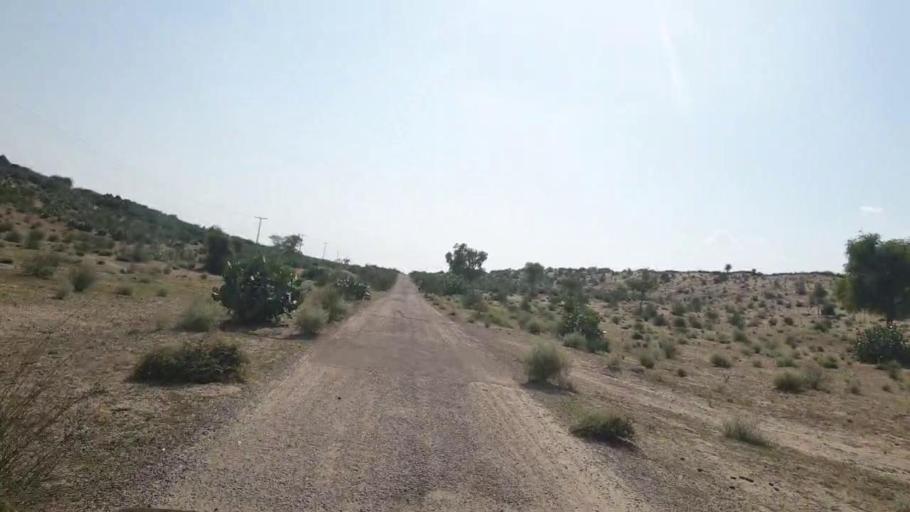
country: PK
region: Sindh
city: Chor
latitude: 25.5601
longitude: 70.2254
